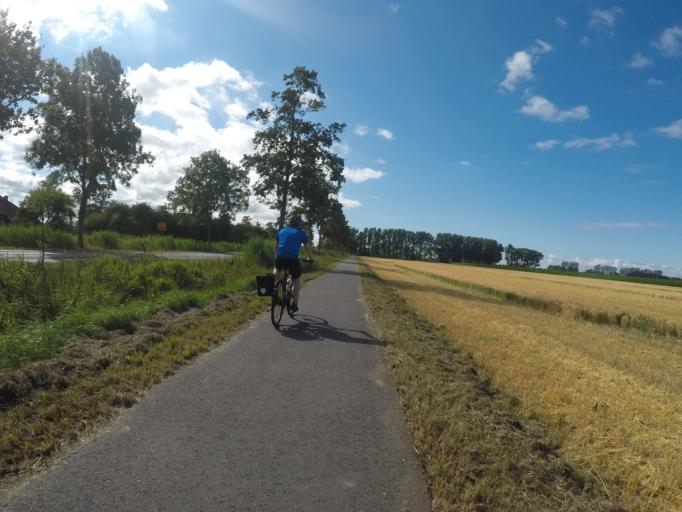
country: DE
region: Lower Saxony
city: Osterbruch
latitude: 53.7836
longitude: 8.9411
